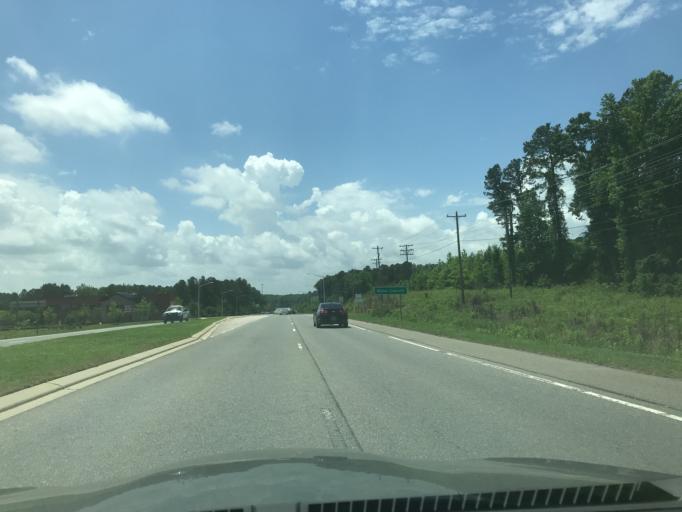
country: US
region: North Carolina
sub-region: Wake County
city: Morrisville
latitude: 35.8685
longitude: -78.8923
